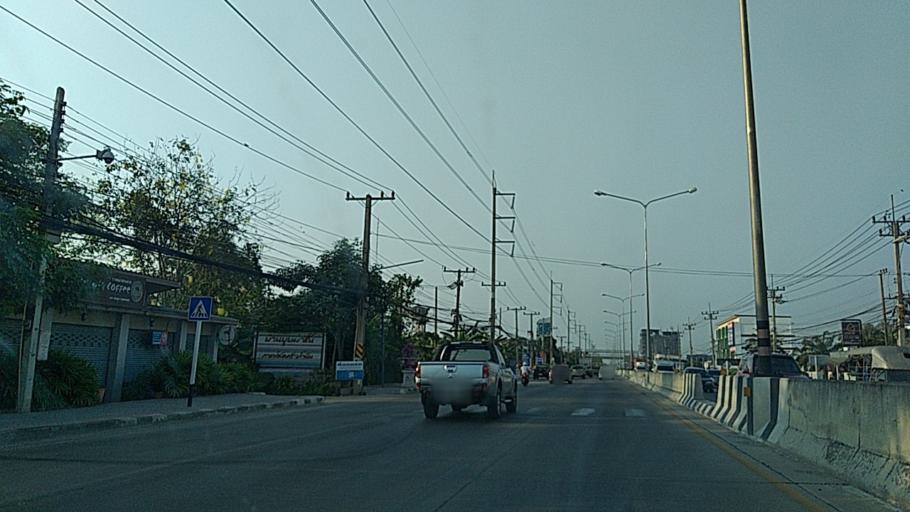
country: TH
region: Phra Nakhon Si Ayutthaya
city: Ban Bang Kadi Pathum Thani
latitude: 13.9838
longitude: 100.5506
